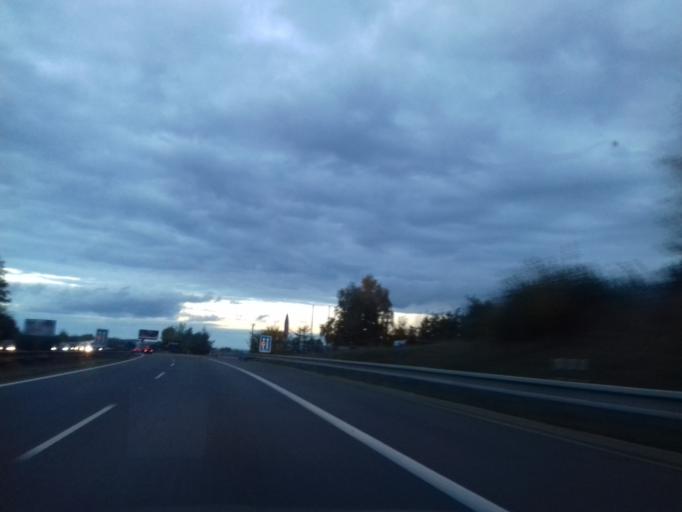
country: CZ
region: Central Bohemia
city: Zruc nad Sazavou
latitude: 49.7061
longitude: 15.0858
